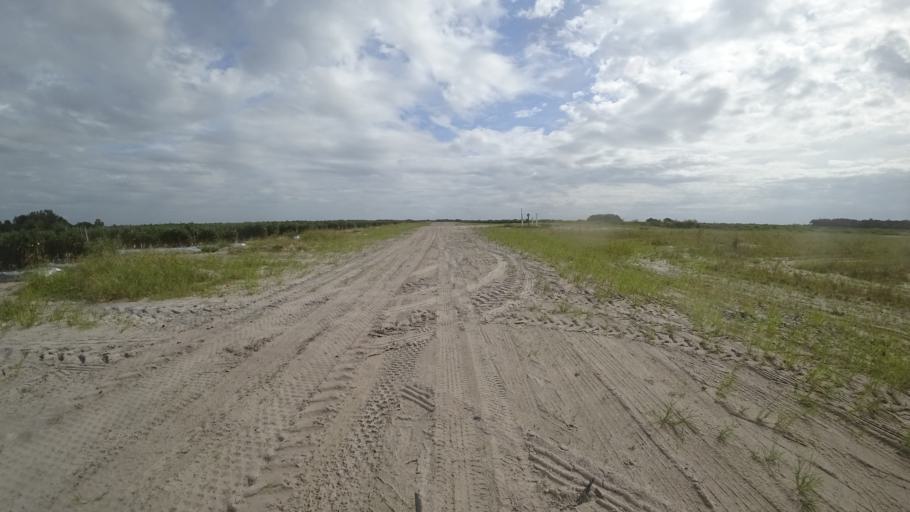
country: US
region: Florida
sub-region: Hillsborough County
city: Wimauma
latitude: 27.5830
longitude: -82.3199
